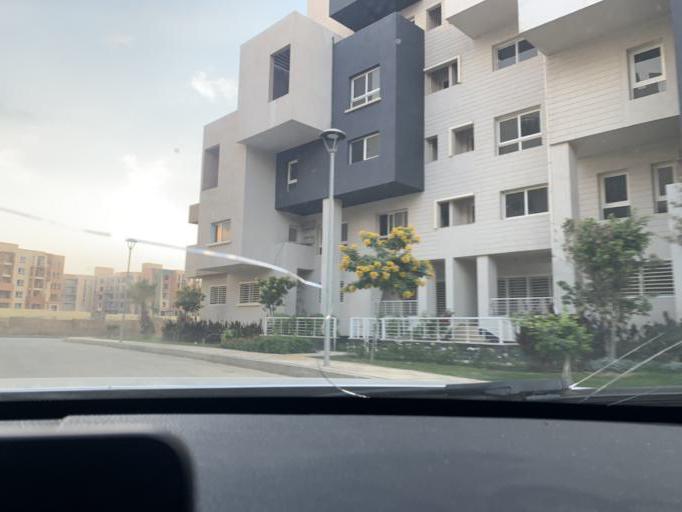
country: EG
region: Muhafazat al Qalyubiyah
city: Al Khankah
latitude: 30.0997
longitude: 31.6528
